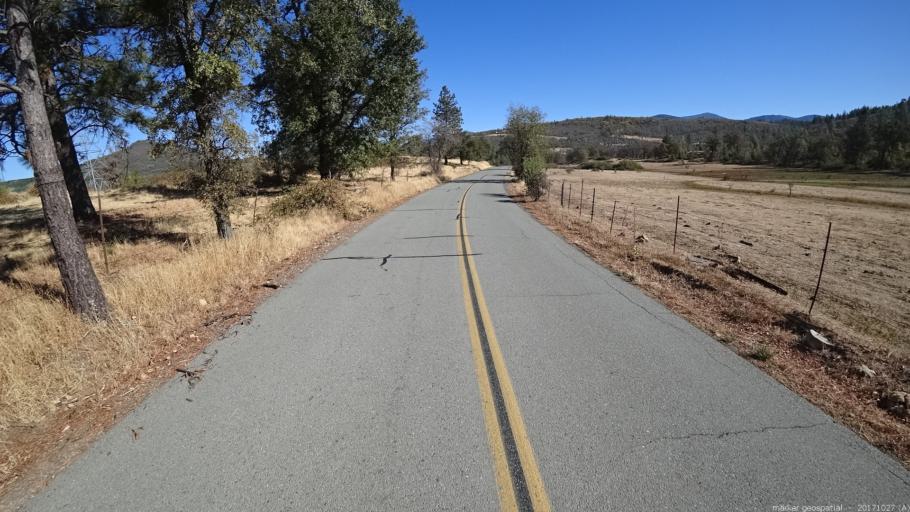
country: US
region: California
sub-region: Shasta County
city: Shingletown
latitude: 40.7698
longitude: -121.9684
